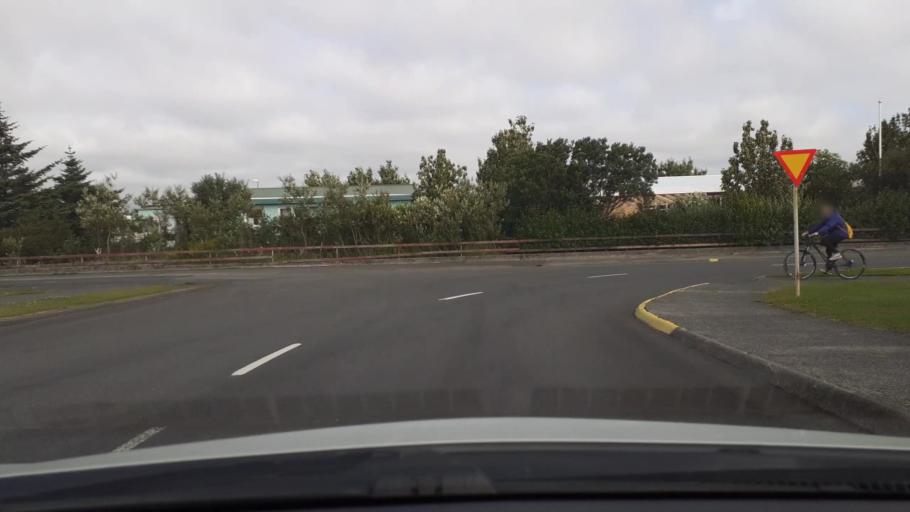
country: IS
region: South
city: THorlakshoefn
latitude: 63.8553
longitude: -21.3911
